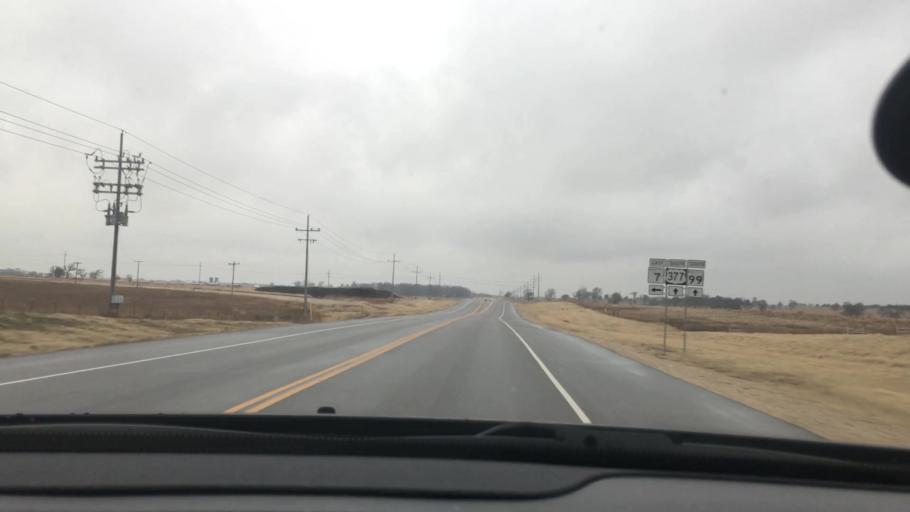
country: US
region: Oklahoma
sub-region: Johnston County
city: Tishomingo
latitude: 34.3649
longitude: -96.6360
